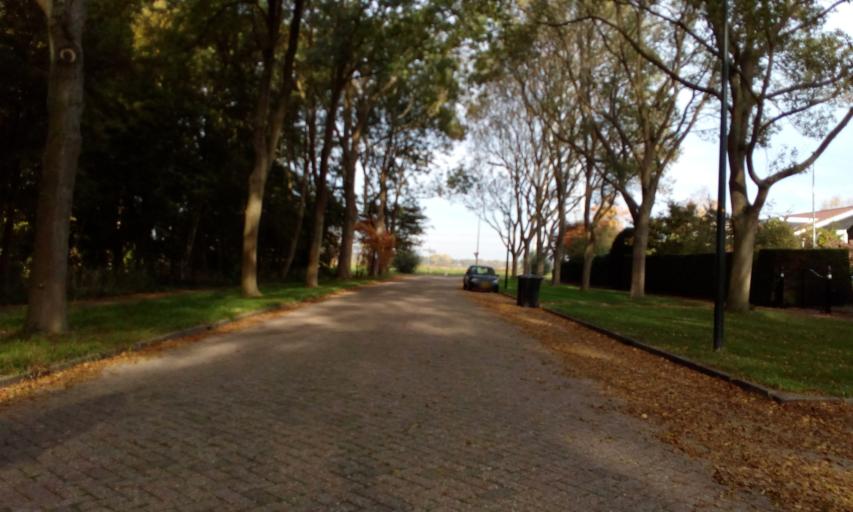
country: NL
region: South Holland
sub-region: Gemeente Leidschendam-Voorburg
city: Voorburg
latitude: 52.0939
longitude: 4.3804
